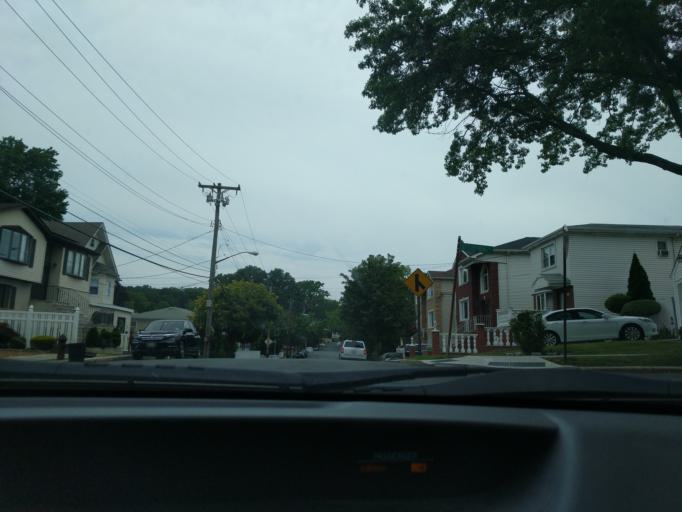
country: US
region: New York
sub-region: Richmond County
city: Staten Island
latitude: 40.5761
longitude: -74.1224
